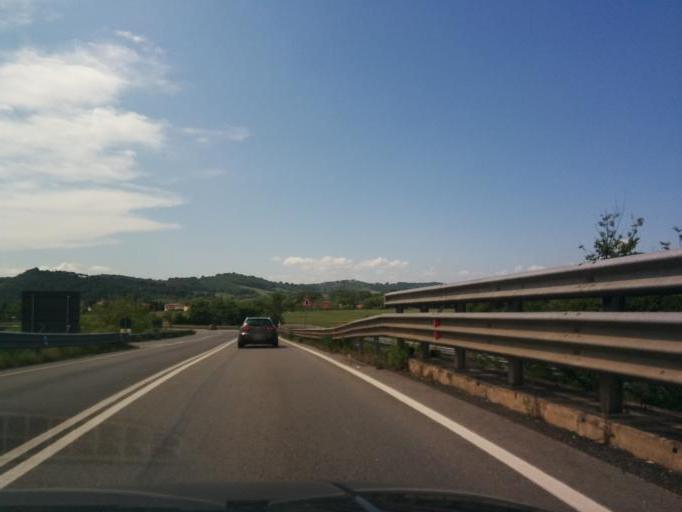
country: IT
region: Tuscany
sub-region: Provincia di Siena
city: Poggibonsi
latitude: 43.4822
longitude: 11.1266
